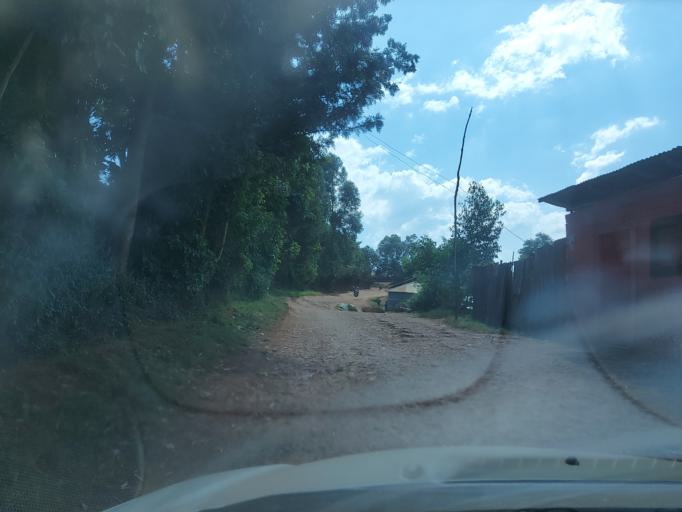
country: CD
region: South Kivu
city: Bukavu
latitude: -2.5077
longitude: 28.8334
